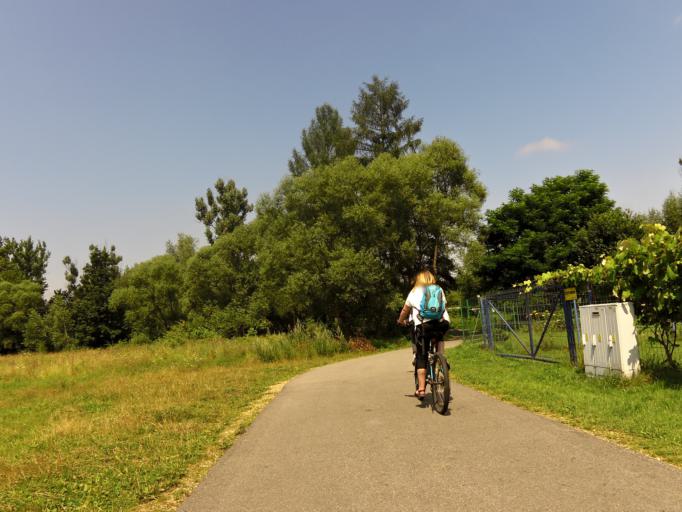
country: PL
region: Silesian Voivodeship
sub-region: Powiat zywiecki
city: Milowka
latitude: 49.5401
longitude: 19.1054
